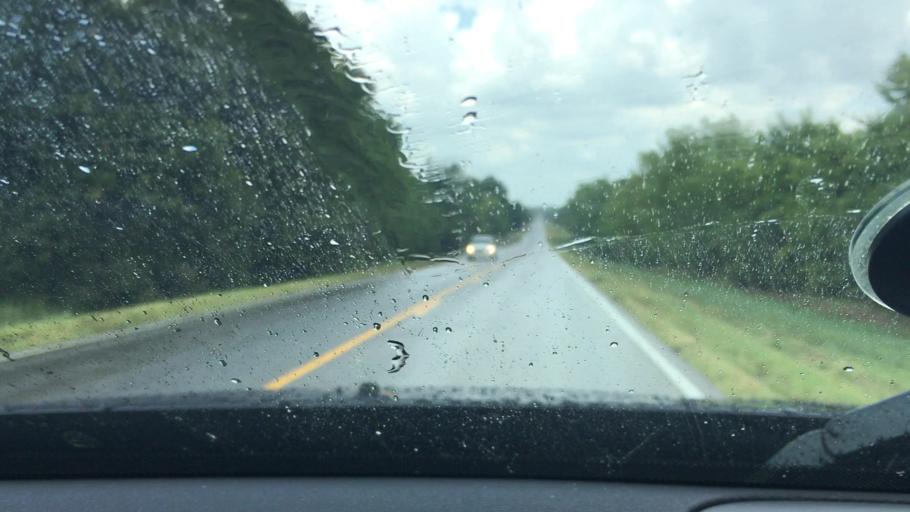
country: US
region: Oklahoma
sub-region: Johnston County
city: Tishomingo
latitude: 34.1954
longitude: -96.7190
